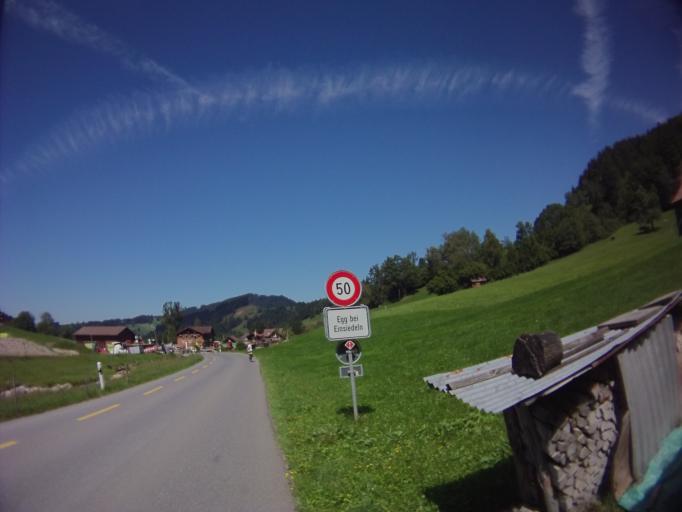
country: CH
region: Schwyz
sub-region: Bezirk Hoefe
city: Feusisberg
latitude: 47.1583
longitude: 8.7871
